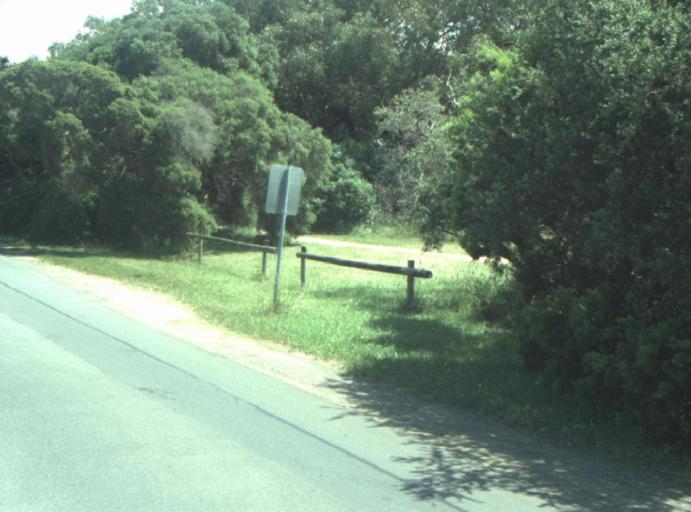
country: AU
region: Victoria
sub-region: Greater Geelong
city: Leopold
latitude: -38.2751
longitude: 144.4939
